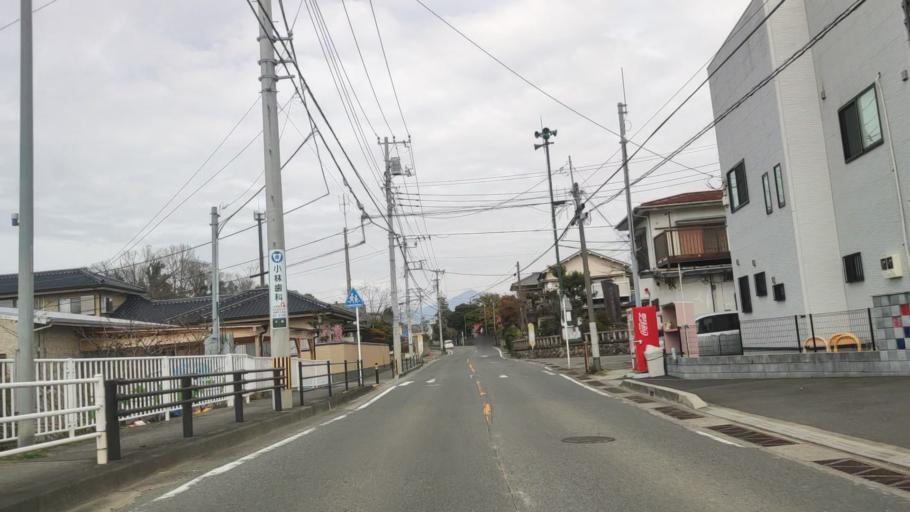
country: JP
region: Kanagawa
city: Ninomiya
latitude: 35.3029
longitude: 139.2268
